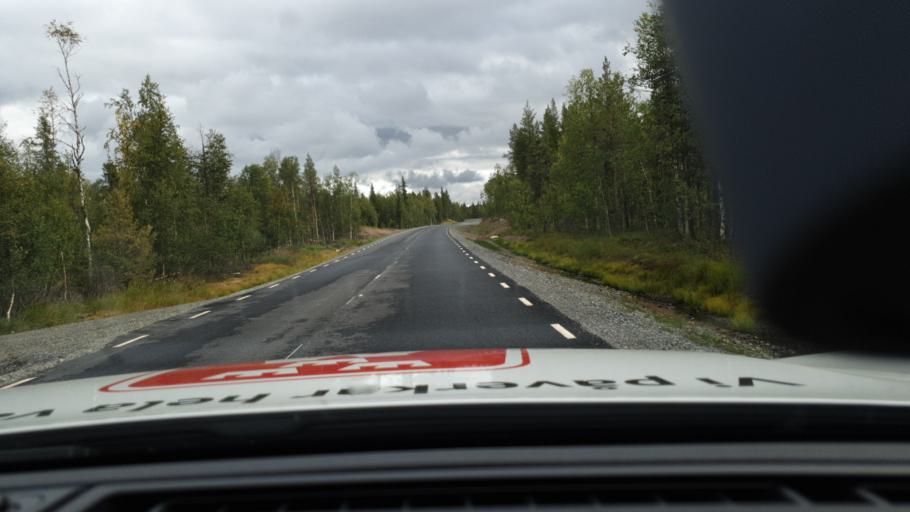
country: SE
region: Norrbotten
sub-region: Gallivare Kommun
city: Gaellivare
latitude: 66.8675
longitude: 21.1930
